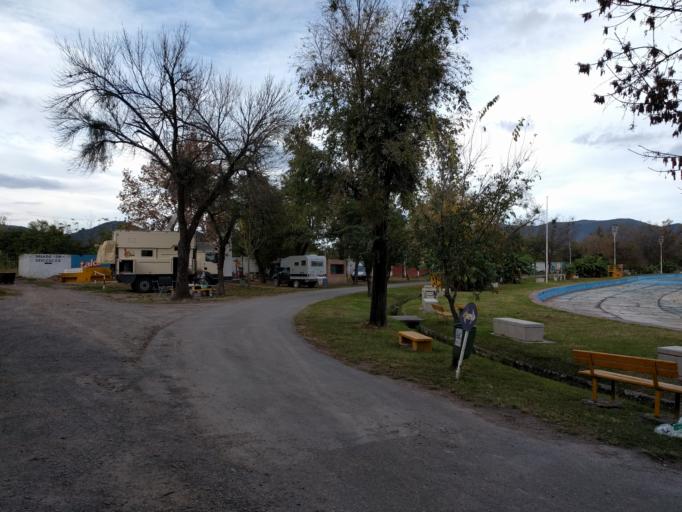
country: AR
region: Salta
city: Salta
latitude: -24.8127
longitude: -65.4189
